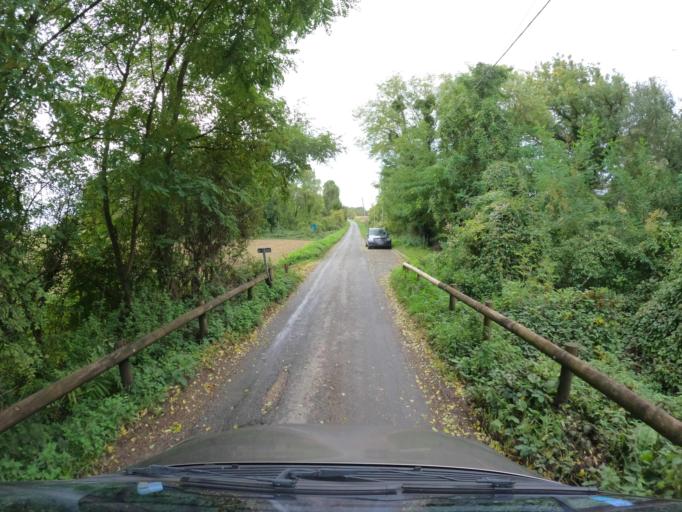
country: FR
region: Ile-de-France
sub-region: Departement de Seine-et-Marne
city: Montry
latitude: 48.8759
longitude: 2.8256
